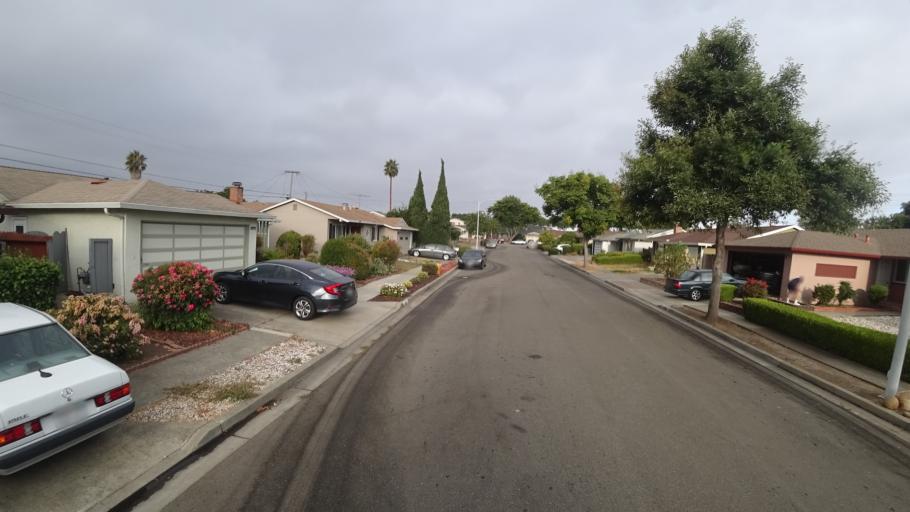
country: US
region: California
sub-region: Alameda County
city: Hayward
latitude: 37.6451
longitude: -122.0971
